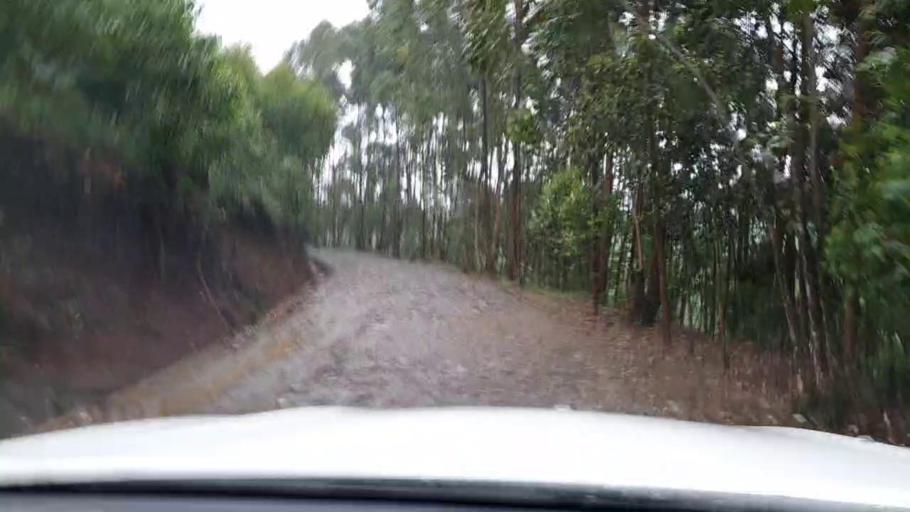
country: RW
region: Western Province
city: Cyangugu
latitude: -2.4669
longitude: 29.0347
